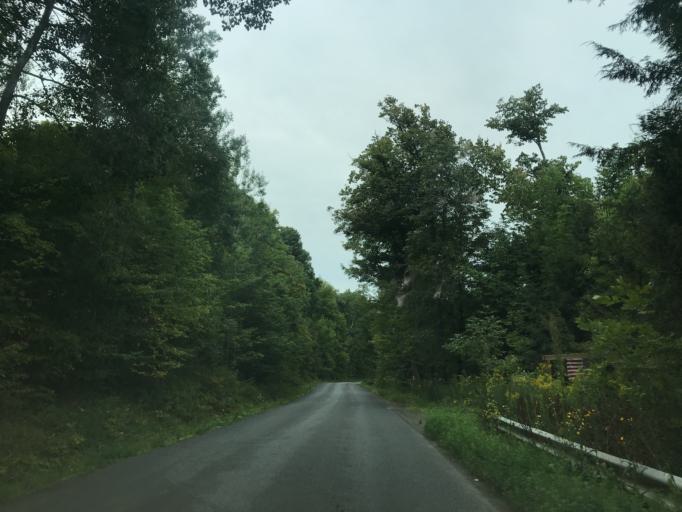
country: US
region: New York
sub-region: Otsego County
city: Worcester
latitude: 42.5899
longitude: -74.7111
